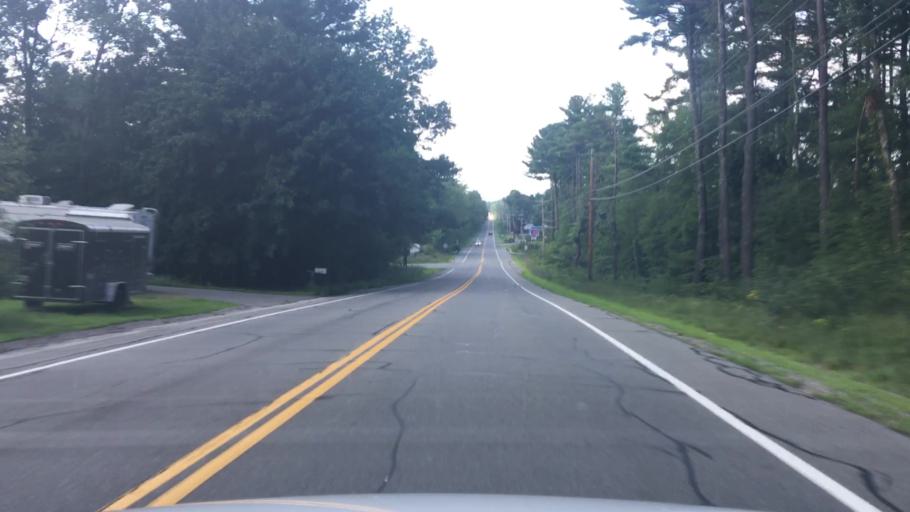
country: US
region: New Hampshire
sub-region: Rockingham County
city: Auburn
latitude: 42.9454
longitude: -71.3489
